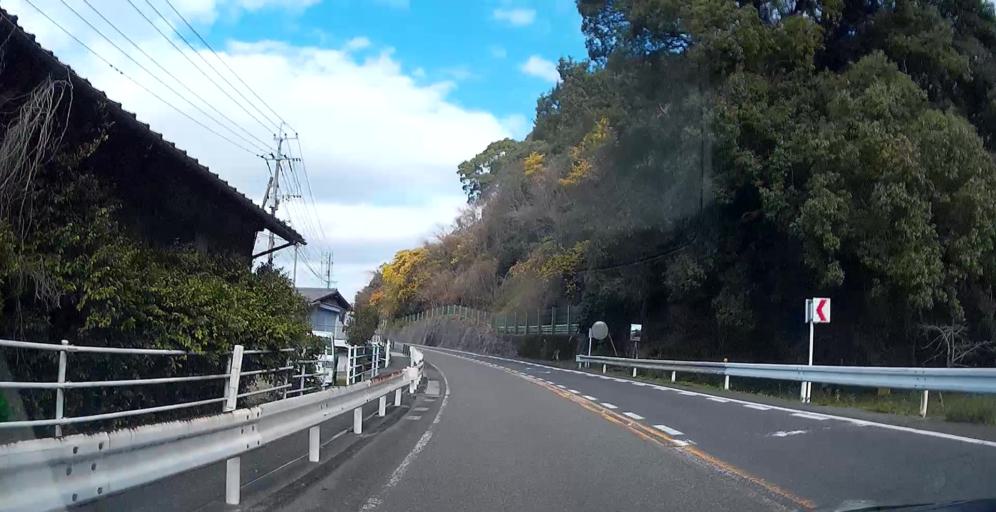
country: JP
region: Kumamoto
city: Yatsushiro
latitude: 32.4276
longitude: 130.5664
